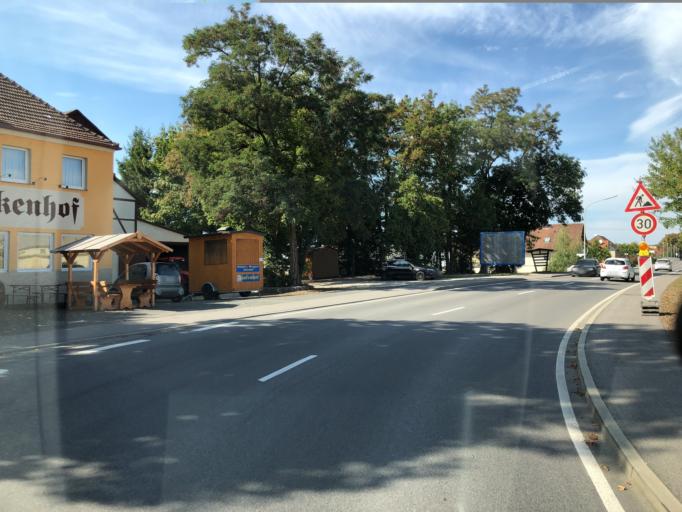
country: DE
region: Bavaria
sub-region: Upper Franconia
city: Michelau
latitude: 50.1558
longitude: 11.1163
